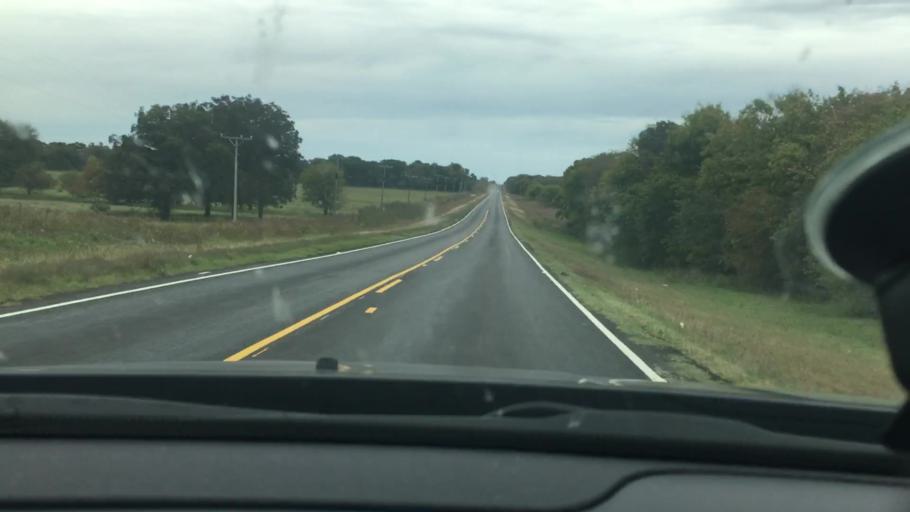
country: US
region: Oklahoma
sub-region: Coal County
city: Coalgate
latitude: 34.3991
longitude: -96.4245
